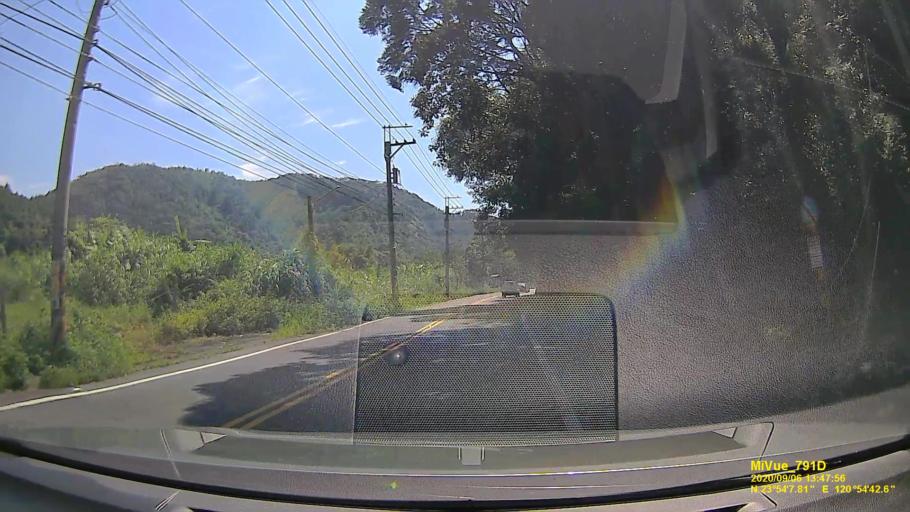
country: TW
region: Taiwan
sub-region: Nantou
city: Puli
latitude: 23.9022
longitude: 120.9118
